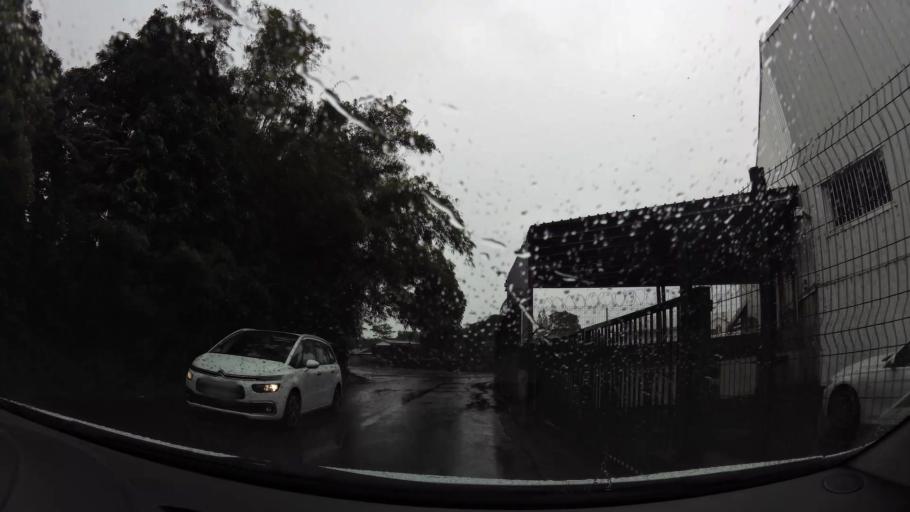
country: RE
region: Reunion
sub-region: Reunion
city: Saint-Andre
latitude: -20.9631
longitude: 55.6508
